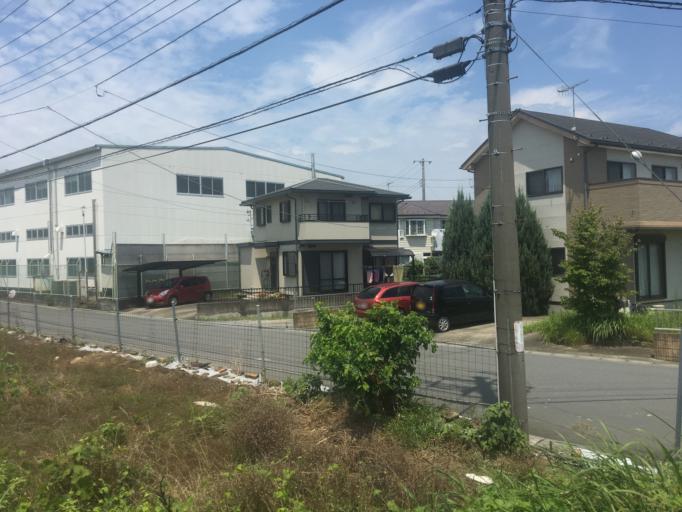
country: JP
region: Saitama
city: Kodamacho-kodamaminami
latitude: 36.1857
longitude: 139.1492
